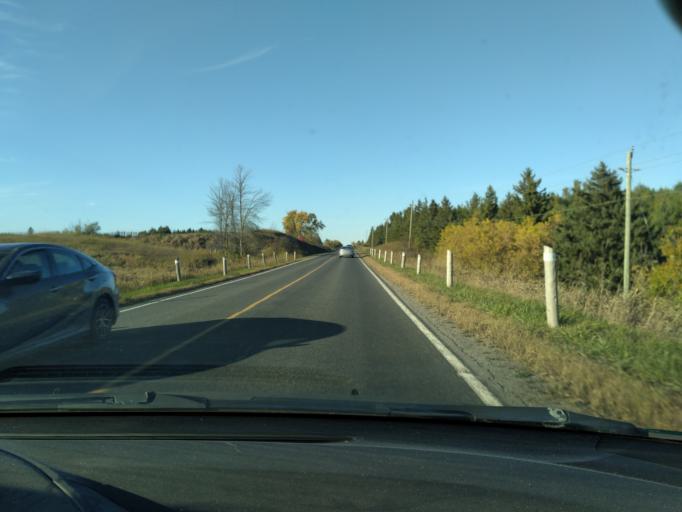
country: CA
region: Ontario
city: Bradford West Gwillimbury
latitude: 43.9414
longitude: -79.7131
